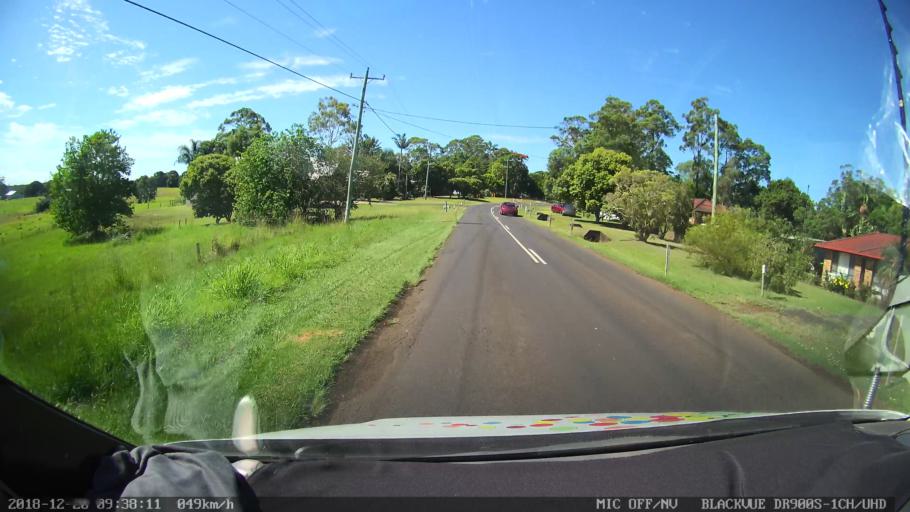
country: AU
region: New South Wales
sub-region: Lismore Municipality
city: Goonellabah
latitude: -28.6888
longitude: 153.3144
